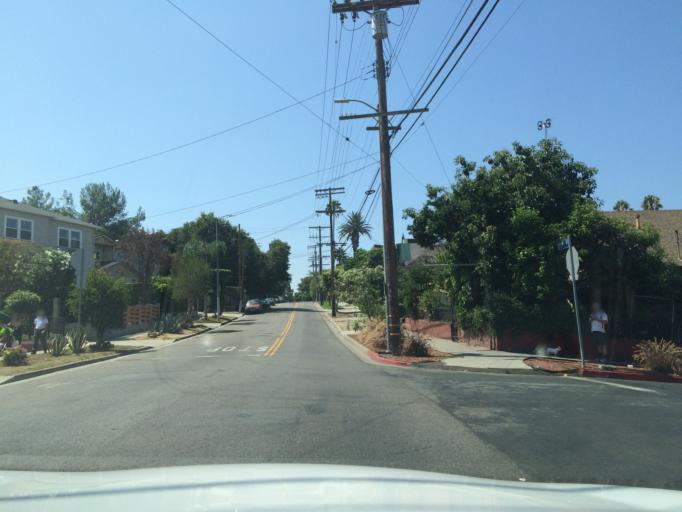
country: US
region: California
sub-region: Los Angeles County
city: Silver Lake
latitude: 34.0868
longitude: -118.2845
